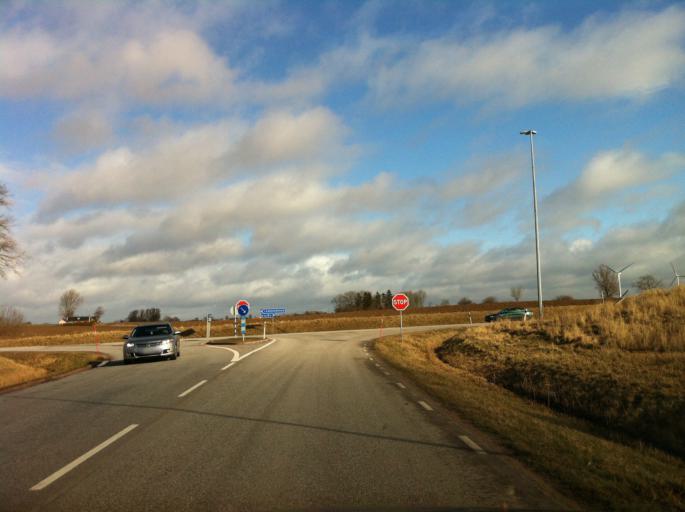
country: SE
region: Skane
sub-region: Landskrona
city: Asmundtorp
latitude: 55.8845
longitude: 13.0033
